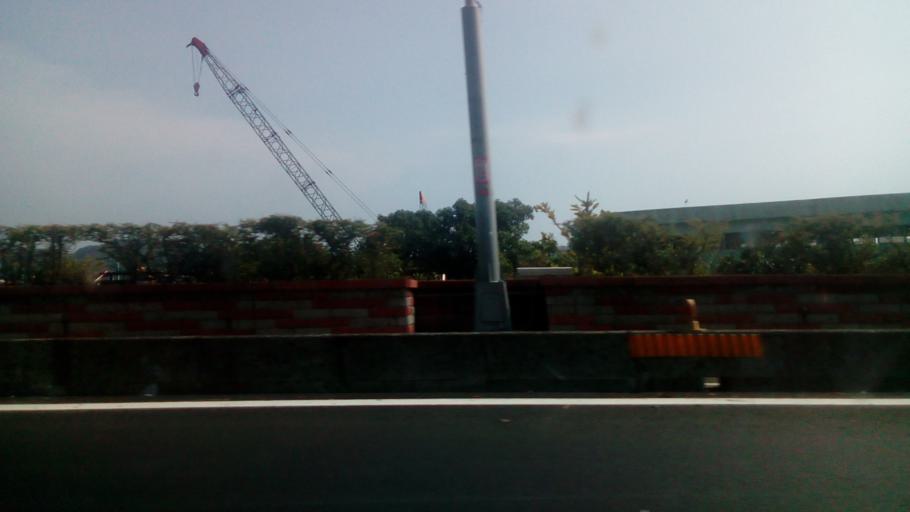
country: TW
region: Taiwan
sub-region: Yilan
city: Yilan
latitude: 24.5876
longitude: 121.8637
